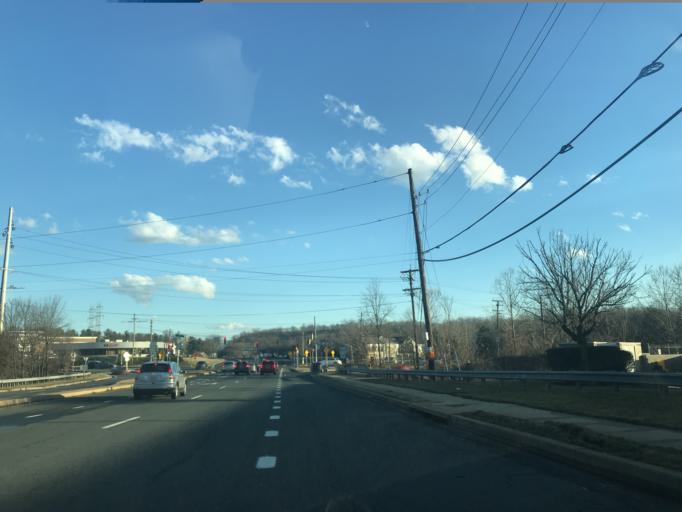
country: US
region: Maryland
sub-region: Prince George's County
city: Woodmore
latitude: 38.9014
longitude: -76.7935
